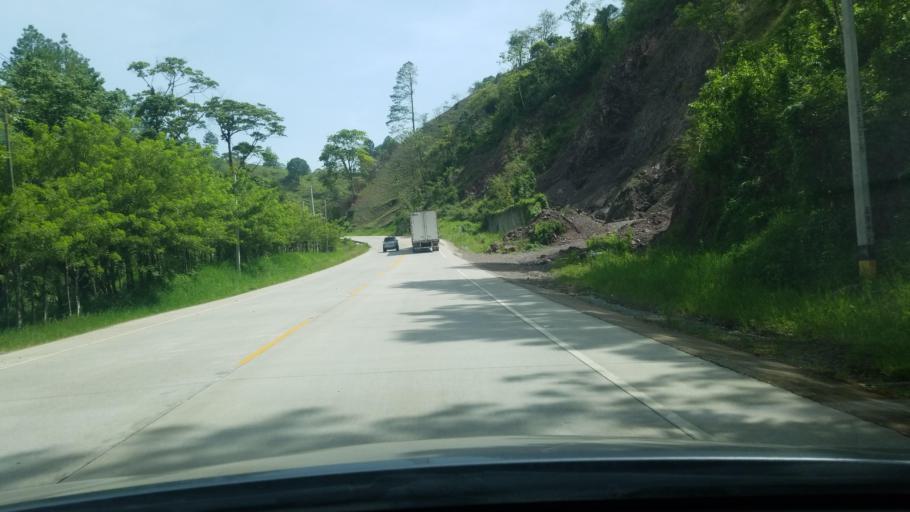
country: HN
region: Copan
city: San Jeronimo
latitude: 14.9637
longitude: -88.8939
